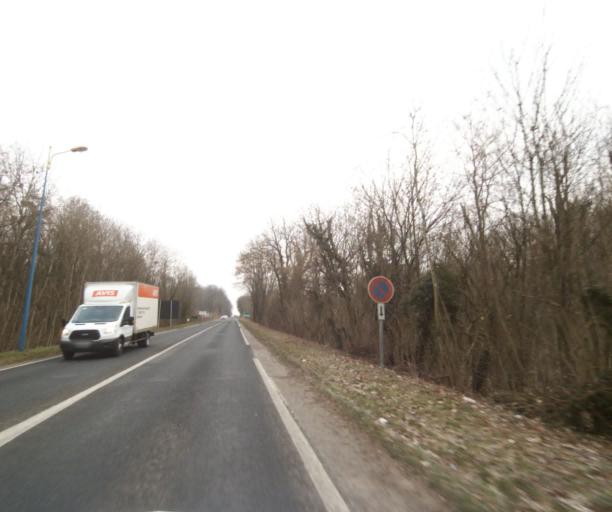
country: FR
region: Champagne-Ardenne
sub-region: Departement de la Haute-Marne
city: Bettancourt-la-Ferree
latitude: 48.6369
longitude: 4.9853
